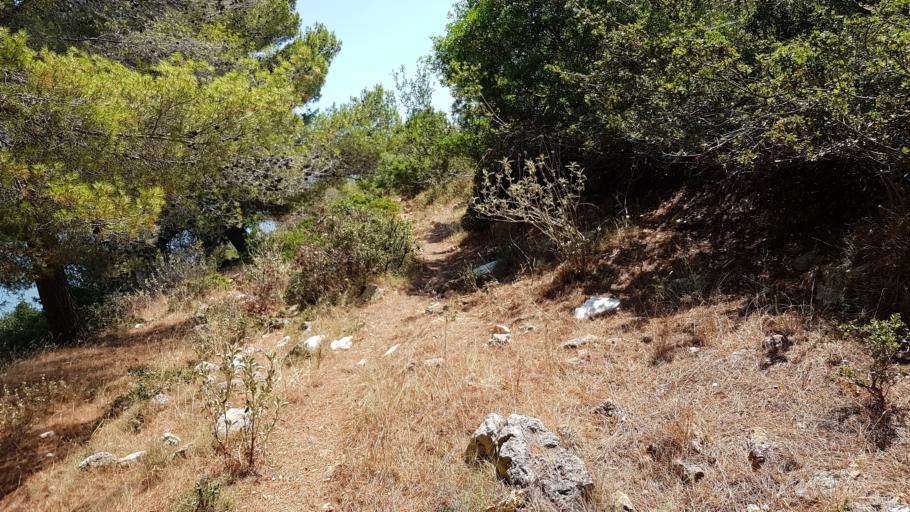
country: AL
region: Vlore
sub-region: Rrethi i Sarandes
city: Xarre
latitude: 39.7480
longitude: 19.9899
